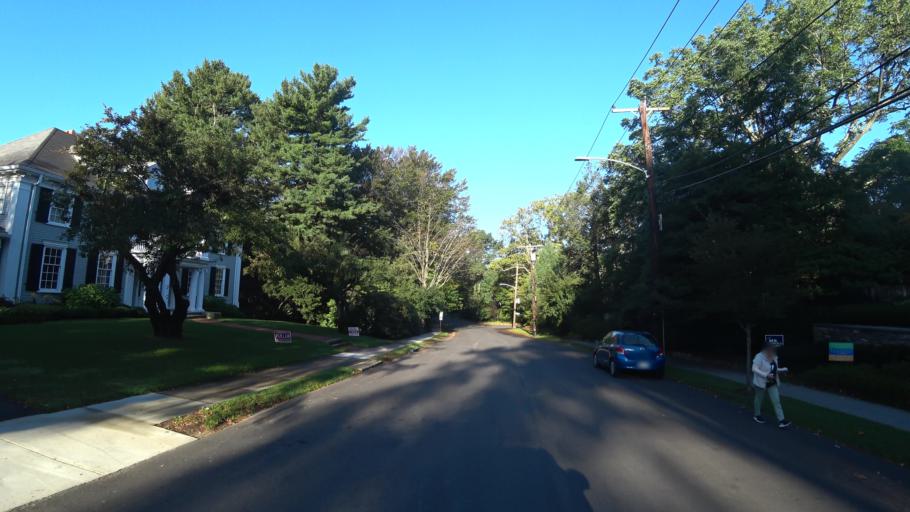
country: US
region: Massachusetts
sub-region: Middlesex County
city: Newton
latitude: 42.3293
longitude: -71.1720
